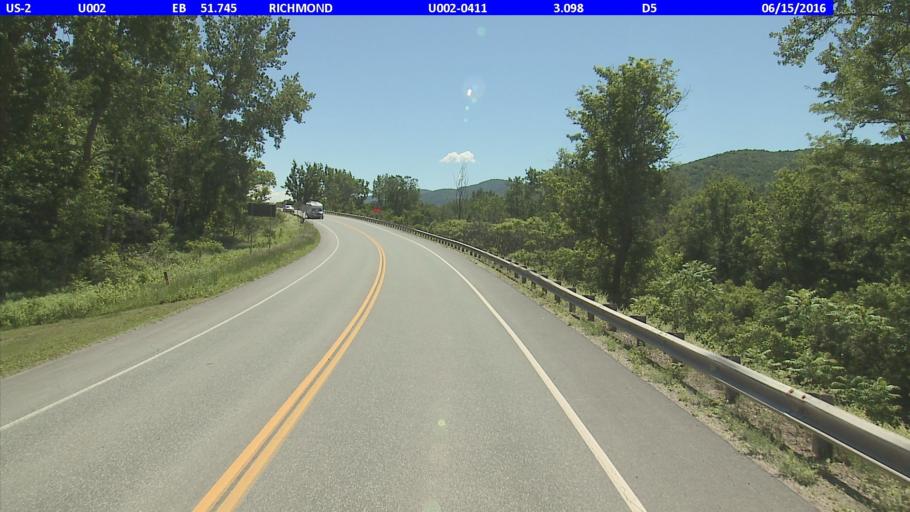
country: US
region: Vermont
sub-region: Chittenden County
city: Williston
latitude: 44.4015
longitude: -72.9872
